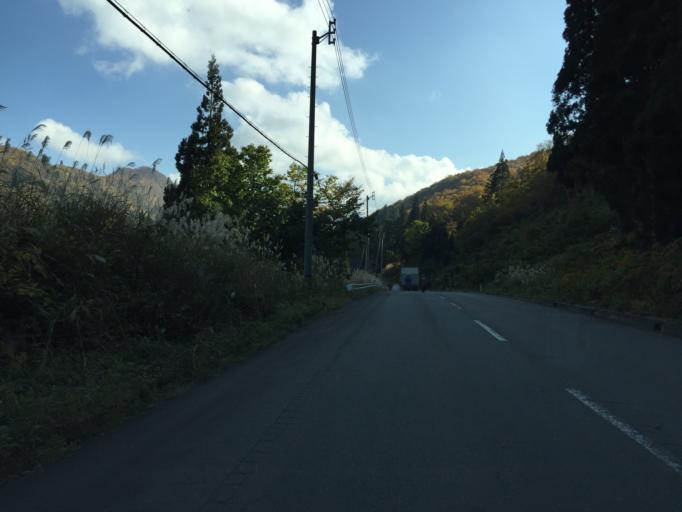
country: JP
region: Yamagata
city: Yonezawa
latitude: 37.8461
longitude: 139.9964
